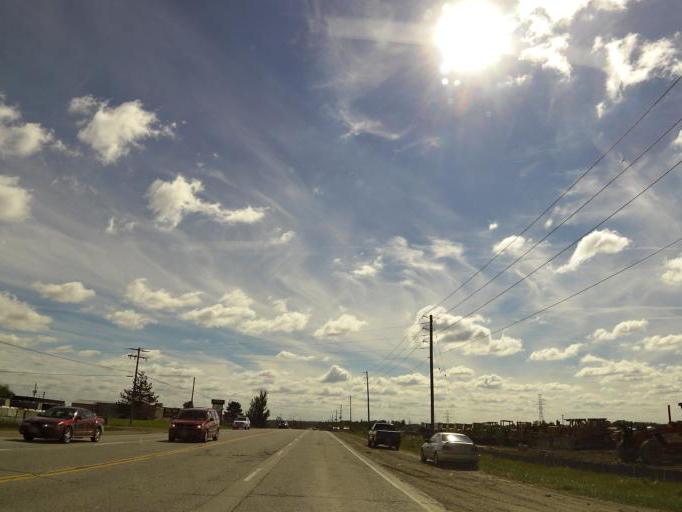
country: CA
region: Ontario
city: London
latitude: 42.9299
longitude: -81.2794
